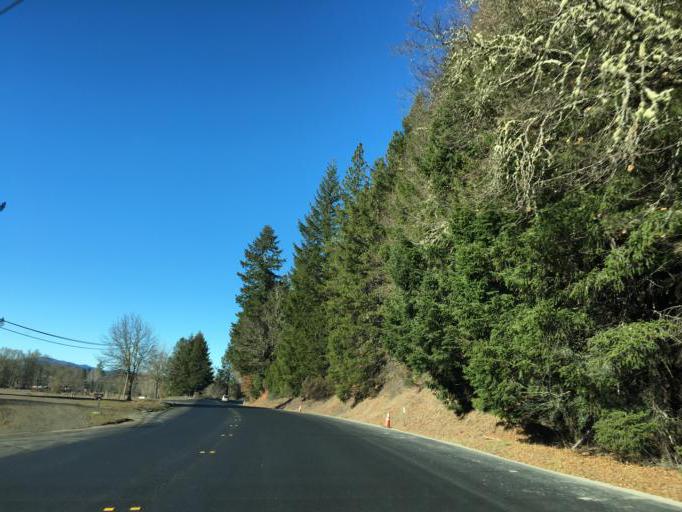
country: US
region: California
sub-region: Mendocino County
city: Laytonville
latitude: 39.6565
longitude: -123.4765
